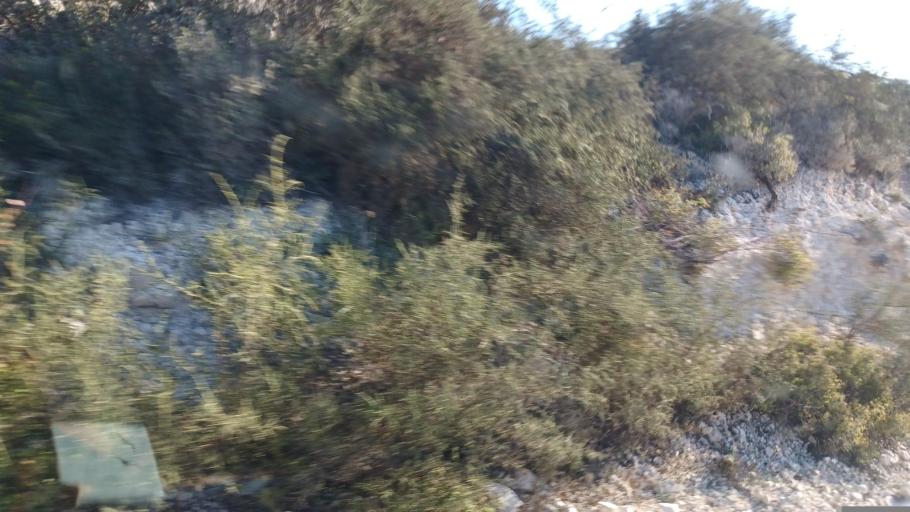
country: CY
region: Pafos
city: Polis
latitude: 34.9805
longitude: 32.5156
